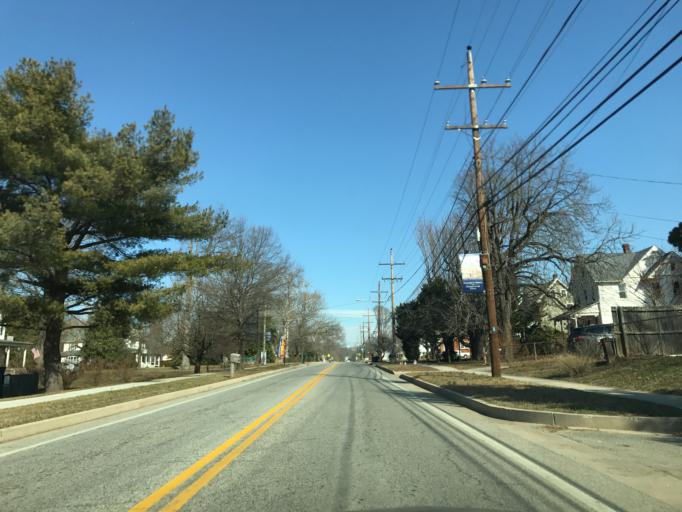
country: US
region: Maryland
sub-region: Cecil County
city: Perryville
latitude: 39.5624
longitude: -76.0712
